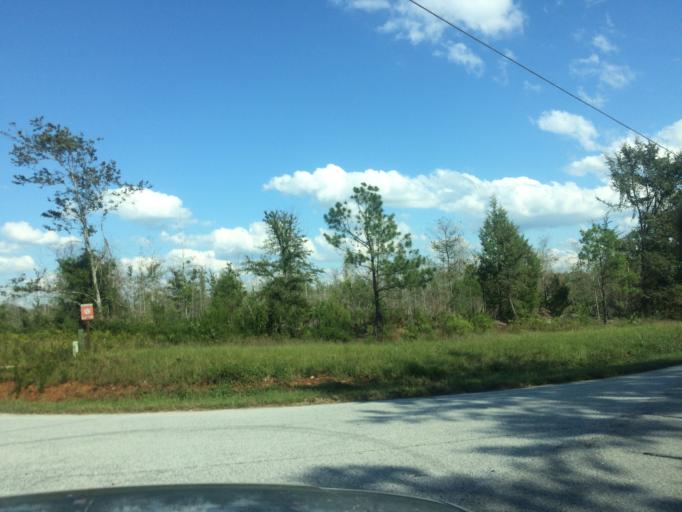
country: US
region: South Carolina
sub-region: Greenwood County
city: Ware Shoals
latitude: 34.4201
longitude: -82.2783
